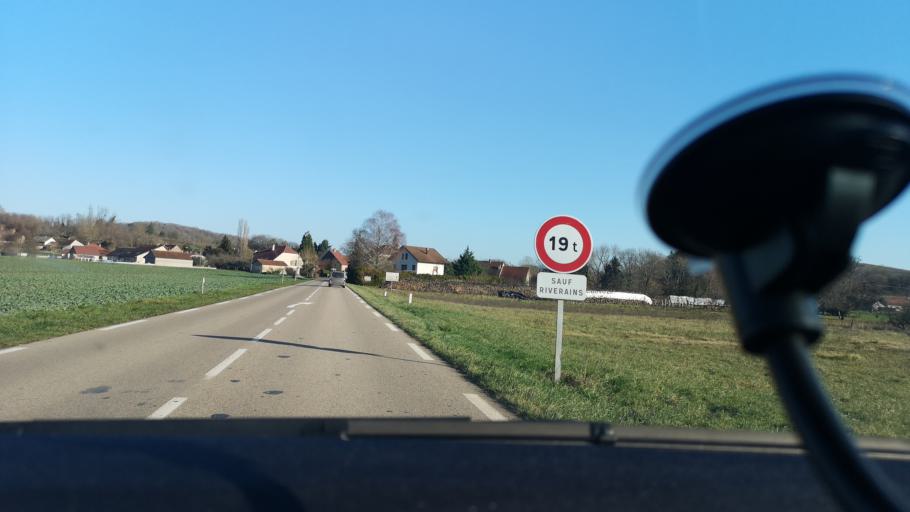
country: FR
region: Franche-Comte
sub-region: Departement du Jura
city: Bletterans
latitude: 46.7607
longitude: 5.5181
